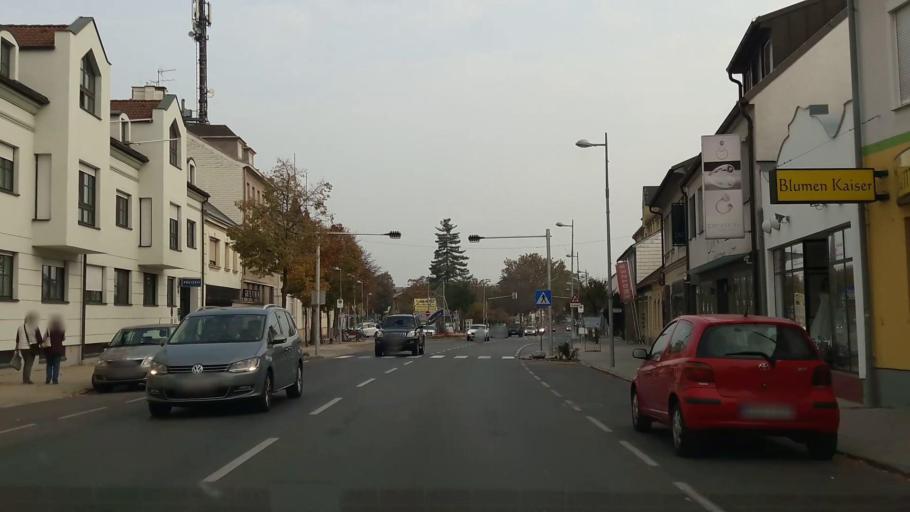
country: AT
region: Burgenland
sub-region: Politischer Bezirk Neusiedl am See
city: Neusiedl am See
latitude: 47.9462
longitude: 16.8471
